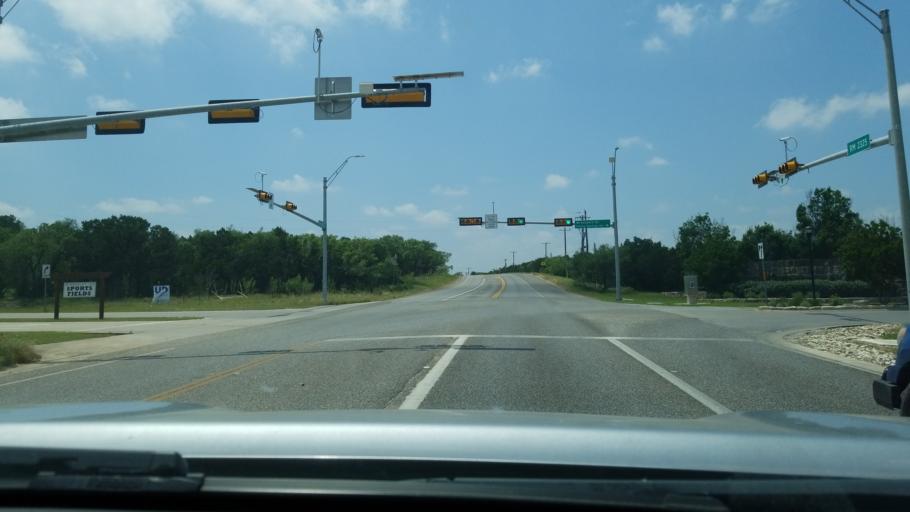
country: US
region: Texas
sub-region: Hays County
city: Woodcreek
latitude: 30.0197
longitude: -98.1379
